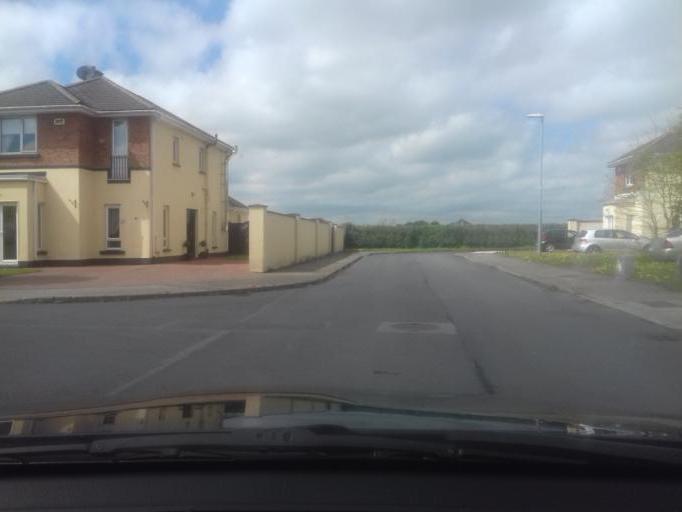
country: IE
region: Leinster
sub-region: Laois
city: Portlaoise
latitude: 53.0479
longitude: -7.3147
